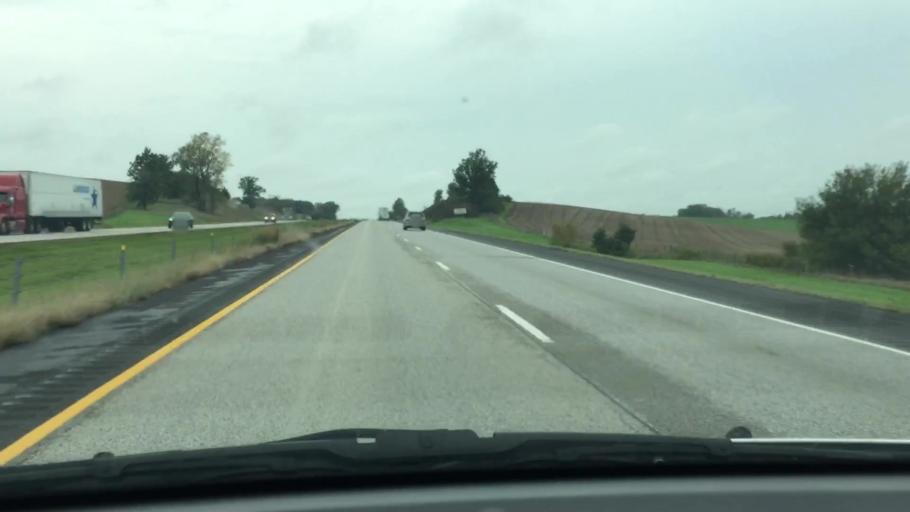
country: US
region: Iowa
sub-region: Johnson County
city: Tiffin
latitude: 41.6955
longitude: -91.7049
